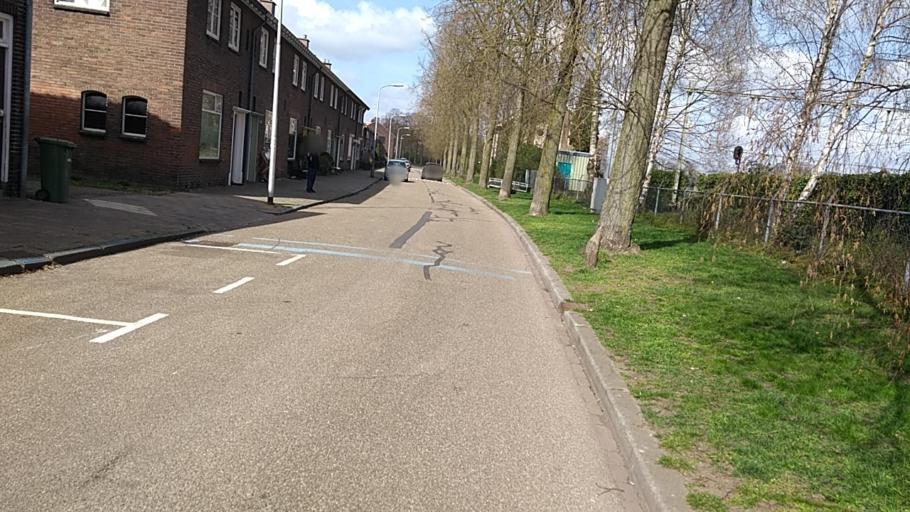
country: NL
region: Overijssel
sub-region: Gemeente Almelo
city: Almelo
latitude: 52.3590
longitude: 6.6518
